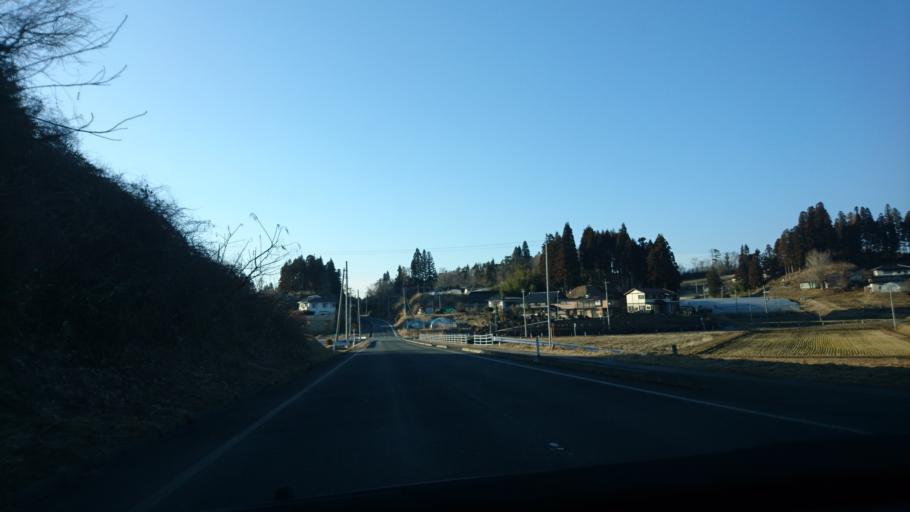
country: JP
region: Iwate
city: Ichinoseki
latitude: 38.9066
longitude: 141.3856
